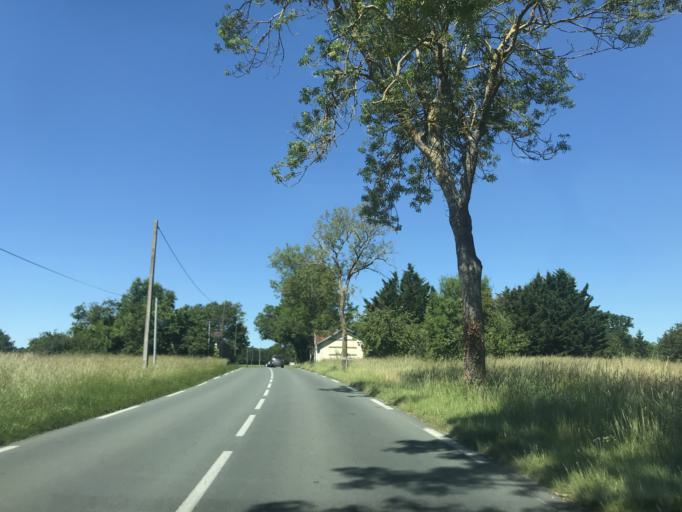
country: FR
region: Poitou-Charentes
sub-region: Departement de la Charente-Maritime
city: Cozes
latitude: 45.5778
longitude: -0.7766
